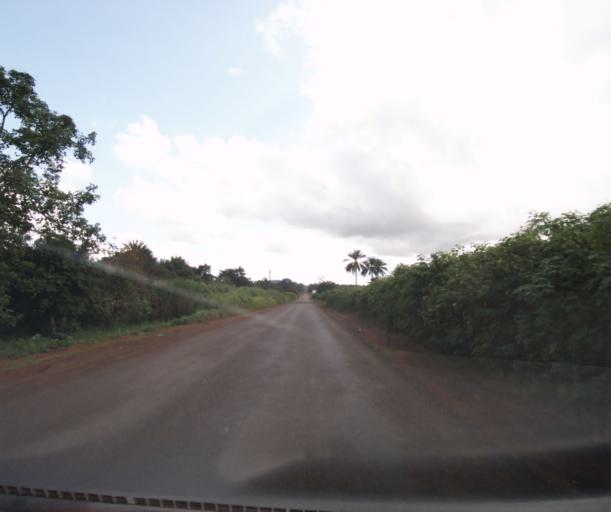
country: CM
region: West
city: Foumban
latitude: 5.6888
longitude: 10.8072
